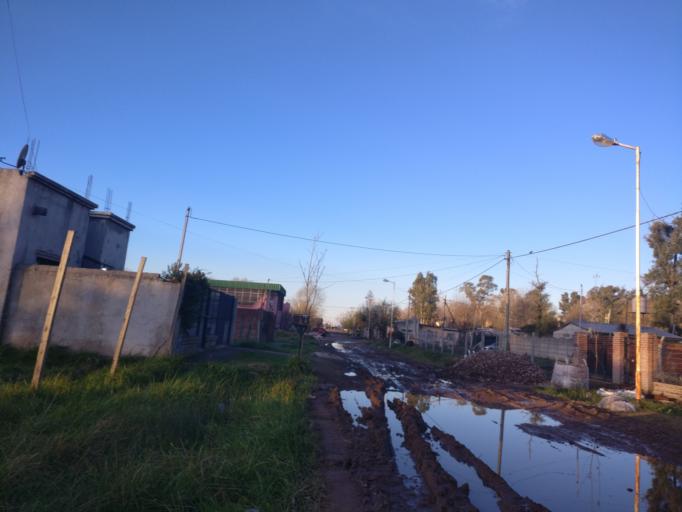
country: AR
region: Buenos Aires
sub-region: Partido de Ezeiza
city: Ezeiza
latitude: -34.9380
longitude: -58.6166
